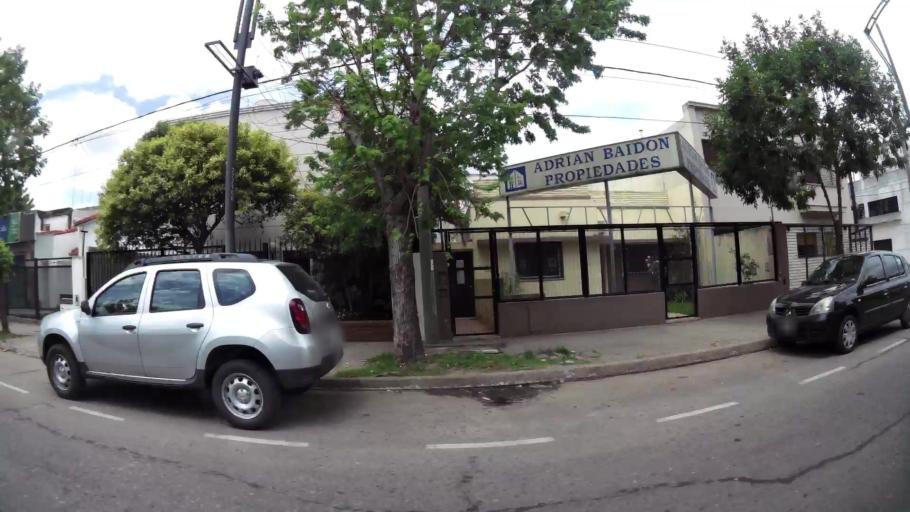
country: AR
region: Santa Fe
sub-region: Departamento de Rosario
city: Rosario
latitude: -32.9721
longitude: -60.6603
